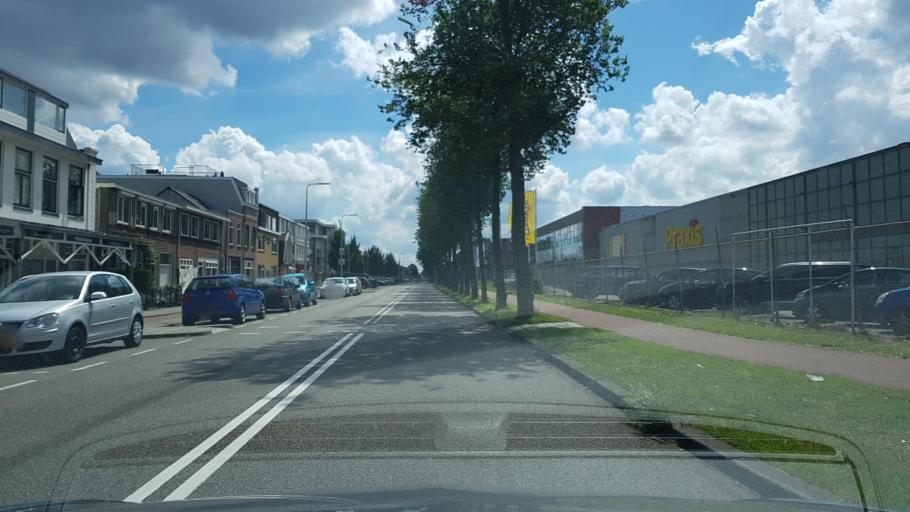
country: NL
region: Utrecht
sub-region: Stichtse Vecht
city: Maarssen
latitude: 52.1136
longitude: 5.0776
